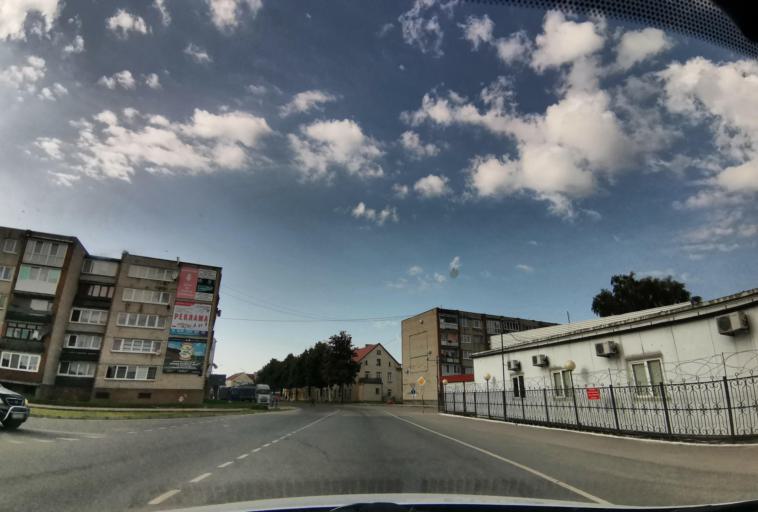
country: RU
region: Kaliningrad
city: Sovetsk
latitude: 55.0820
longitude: 21.9039
